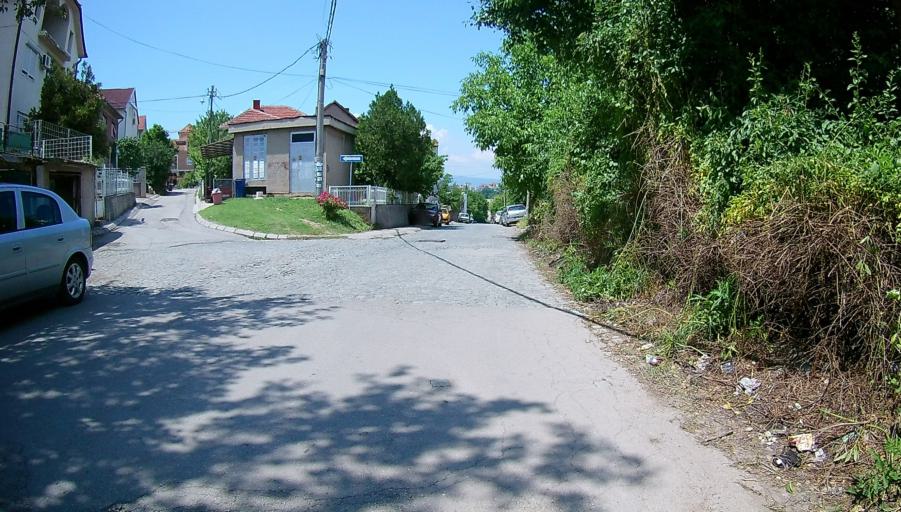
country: RS
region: Central Serbia
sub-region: Nisavski Okrug
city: Nis
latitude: 43.3093
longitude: 21.9144
